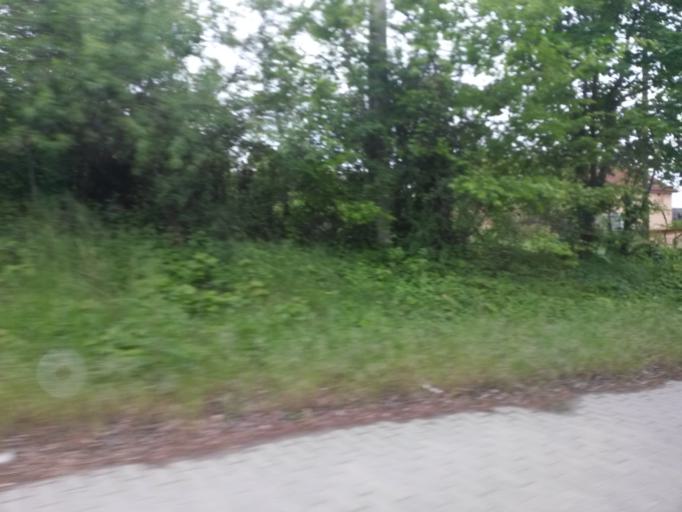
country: HU
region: Budapest
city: Budapest XII. keruelet
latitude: 47.4655
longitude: 19.0031
